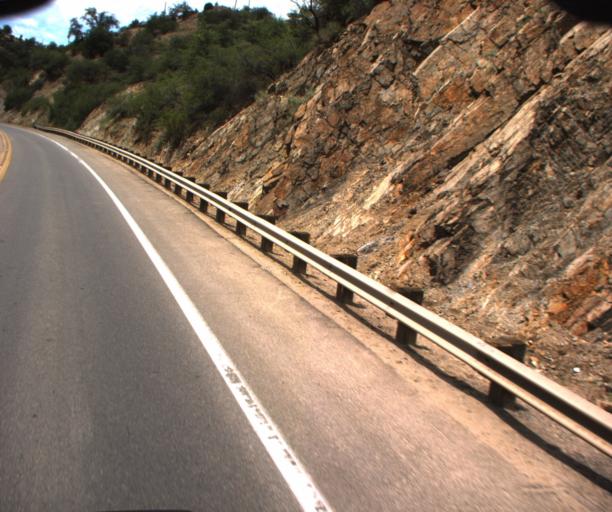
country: US
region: Arizona
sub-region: Gila County
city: Miami
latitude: 33.3900
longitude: -110.8841
